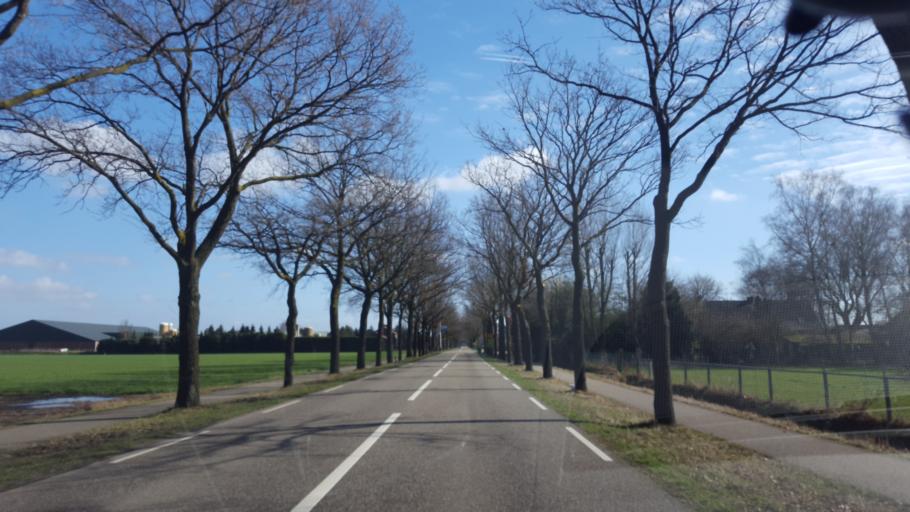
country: NL
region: Limburg
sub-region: Gemeente Weert
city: Weert
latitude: 51.2576
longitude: 5.6534
